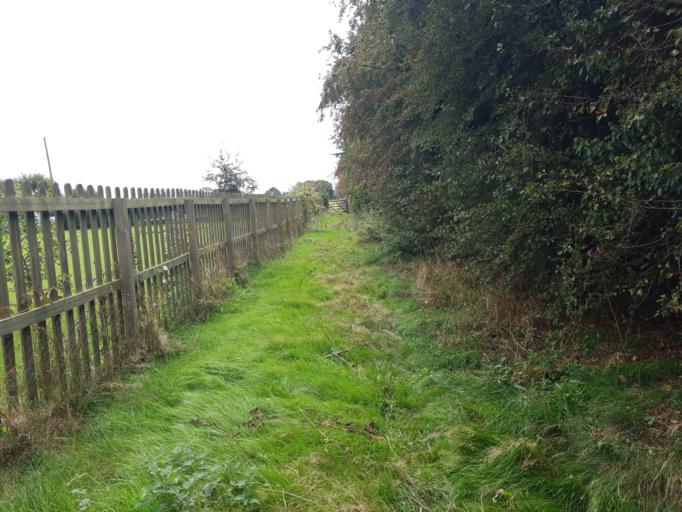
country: GB
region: England
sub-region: Suffolk
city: East Bergholt
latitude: 51.9327
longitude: 0.9917
